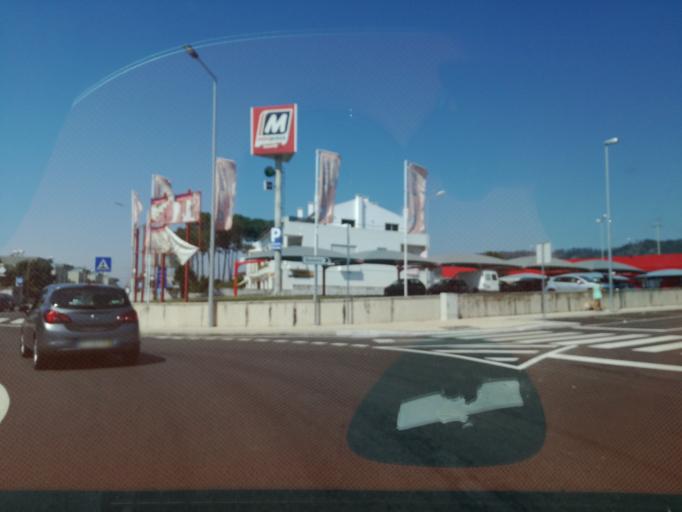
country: PT
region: Braga
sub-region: Esposende
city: Esposende
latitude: 41.5459
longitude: -8.7823
